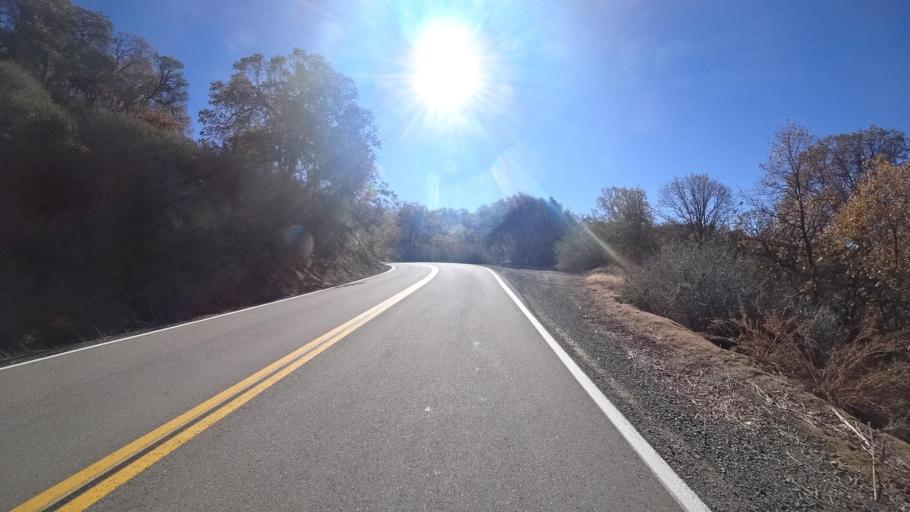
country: US
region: California
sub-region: Kern County
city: Alta Sierra
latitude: 35.7390
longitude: -118.6201
